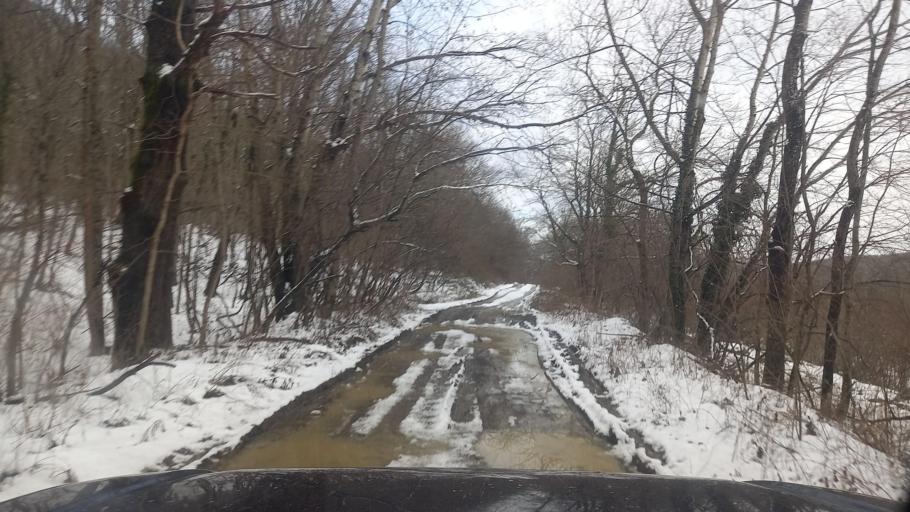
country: RU
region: Krasnodarskiy
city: Smolenskaya
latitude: 44.6887
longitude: 38.8658
